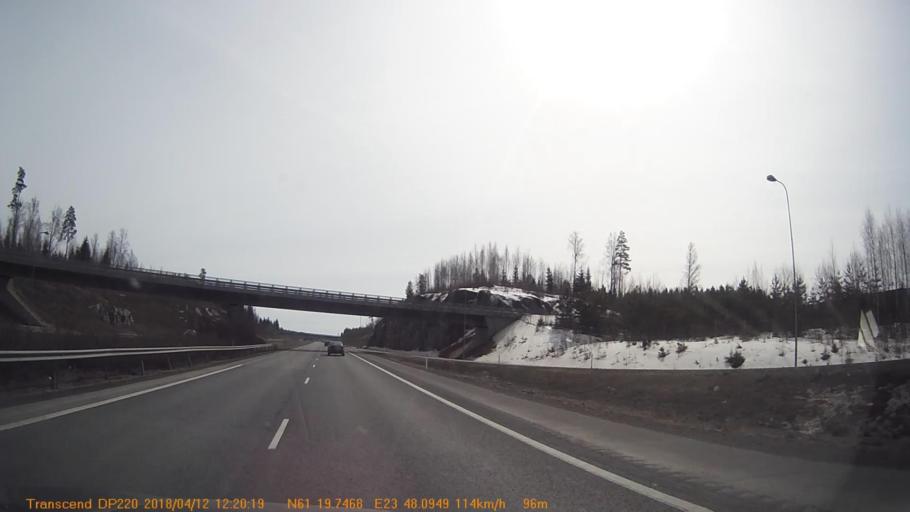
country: FI
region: Pirkanmaa
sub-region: Tampere
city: Lempaeaelae
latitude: 61.3287
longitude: 23.8021
